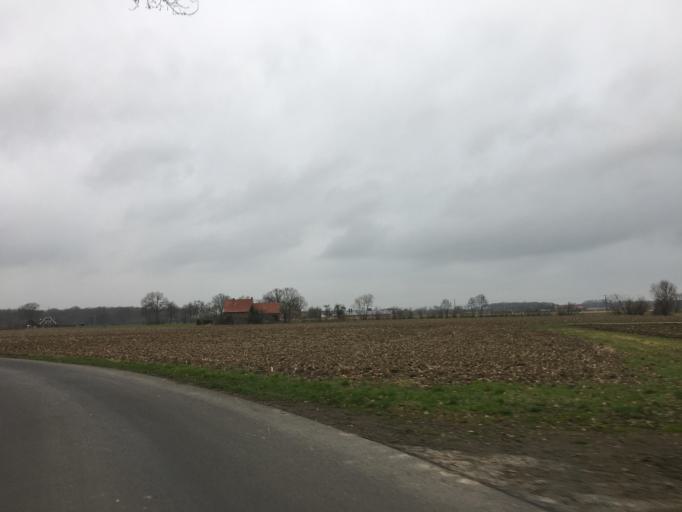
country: DE
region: North Rhine-Westphalia
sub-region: Regierungsbezirk Munster
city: Senden
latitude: 51.8699
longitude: 7.4461
